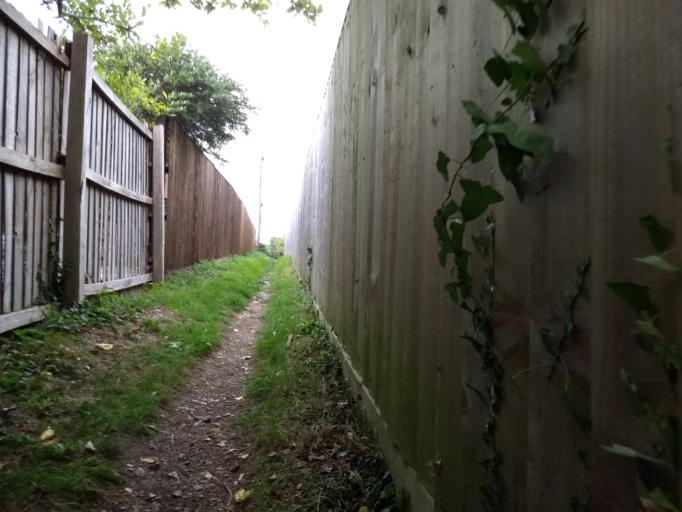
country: GB
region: England
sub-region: Isle of Wight
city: Brading
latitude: 50.6827
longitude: -1.1402
